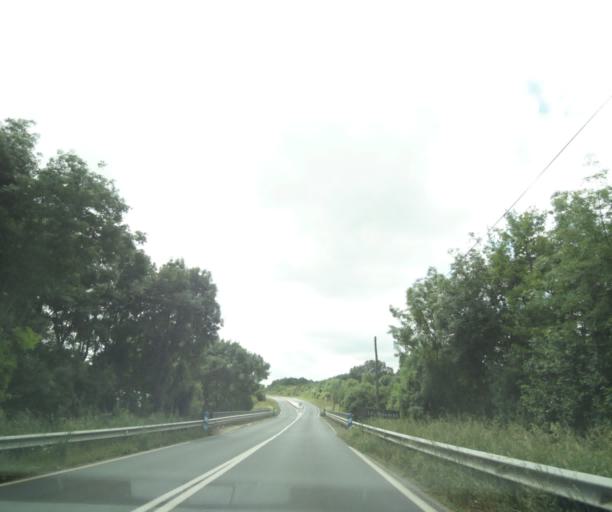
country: FR
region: Poitou-Charentes
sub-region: Departement des Deux-Sevres
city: Saint-Varent
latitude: 46.9154
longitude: -0.1960
